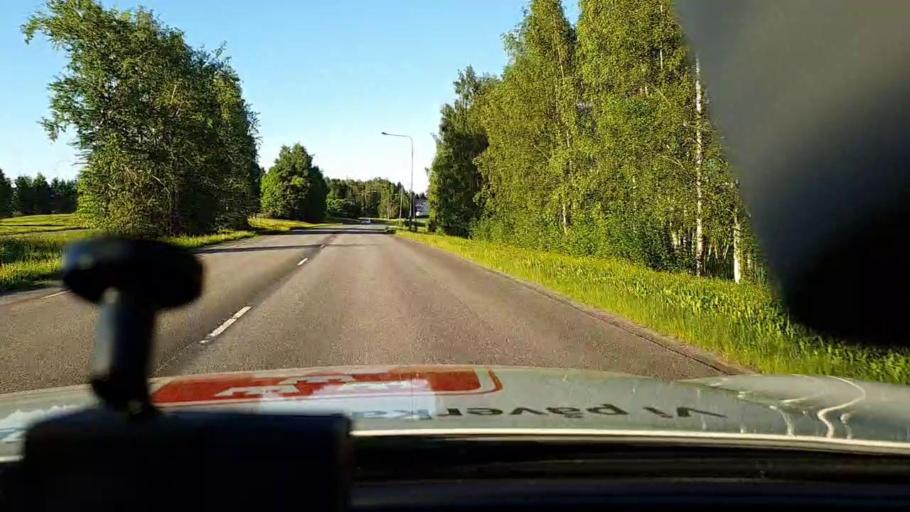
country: SE
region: Norrbotten
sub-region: Lulea Kommun
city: Lulea
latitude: 65.6139
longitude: 22.1420
